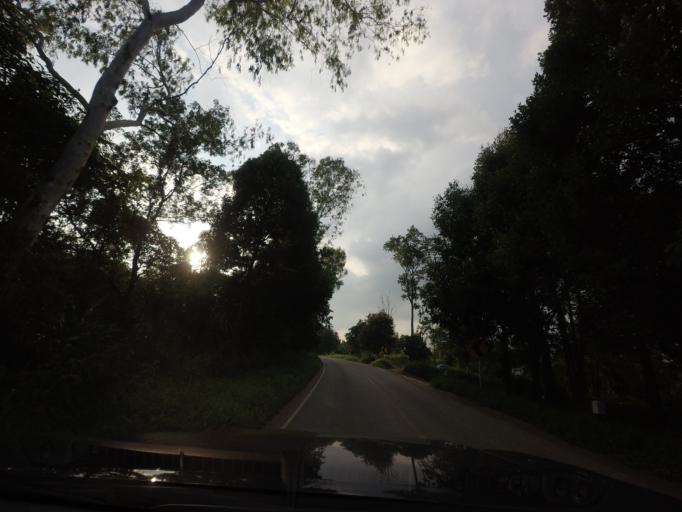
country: TH
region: Loei
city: Dan Sai
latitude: 17.3301
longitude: 101.1140
